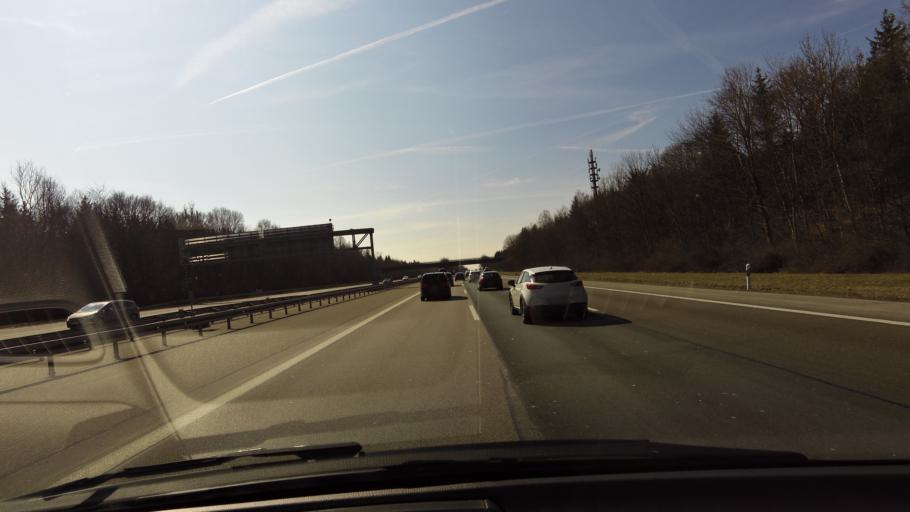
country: DE
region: Bavaria
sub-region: Upper Bavaria
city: Vaterstetten
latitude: 48.1013
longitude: 11.7516
